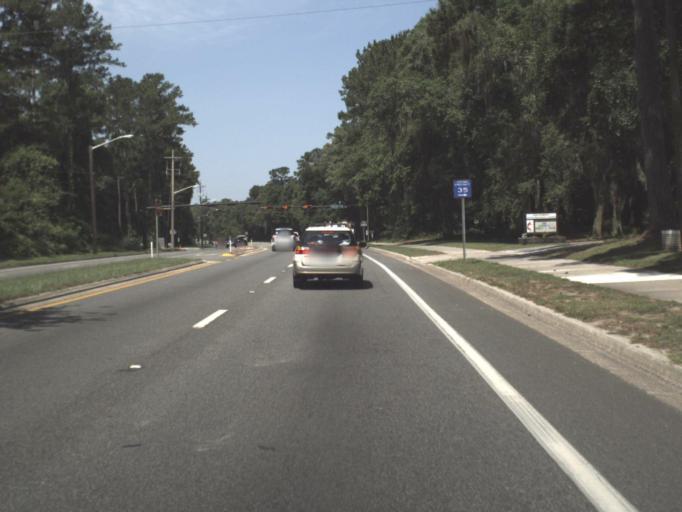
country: US
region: Florida
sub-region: Alachua County
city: Gainesville
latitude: 29.6128
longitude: -82.3576
